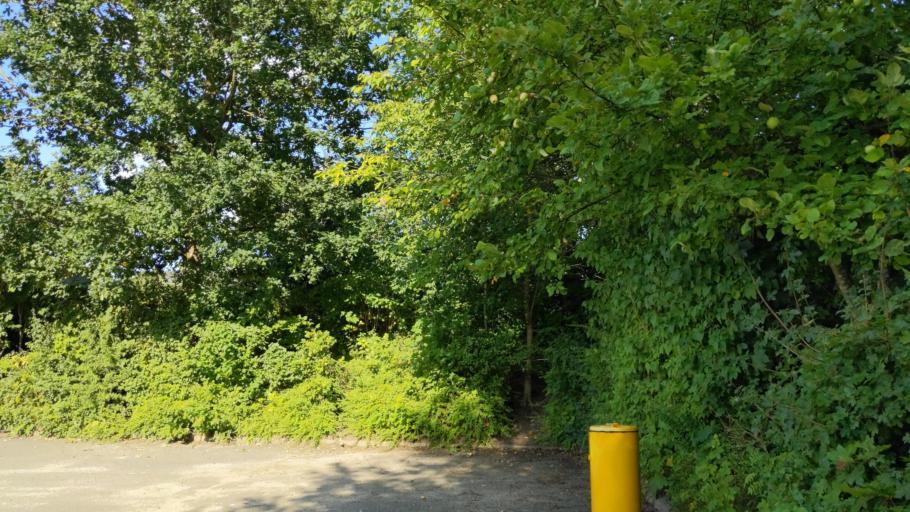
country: DE
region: Schleswig-Holstein
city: Susel
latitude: 54.0778
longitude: 10.7111
